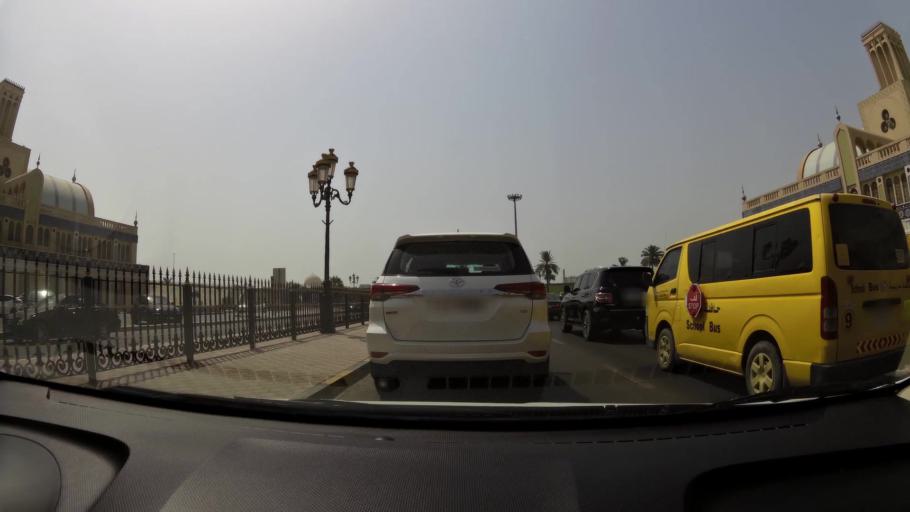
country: AE
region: Ash Shariqah
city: Sharjah
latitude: 25.3478
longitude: 55.3835
